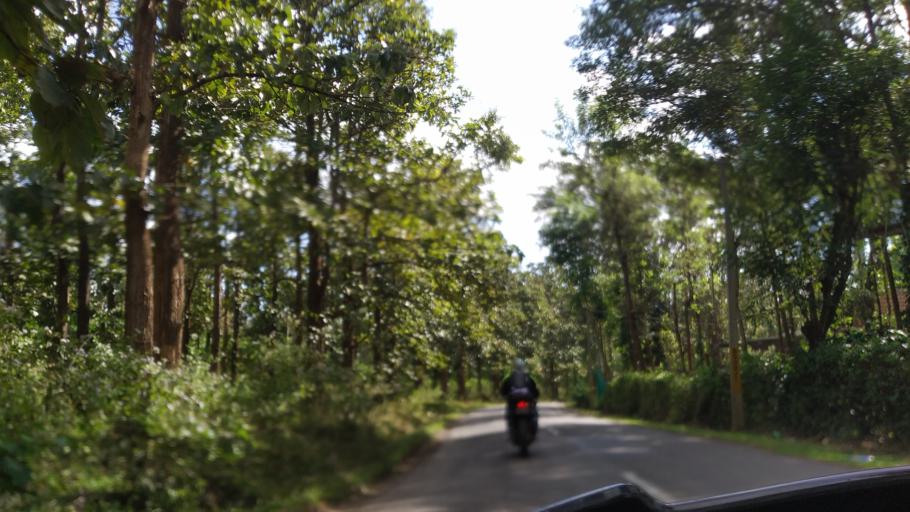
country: IN
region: Kerala
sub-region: Wayanad
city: Panamaram
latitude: 11.9368
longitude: 76.0648
